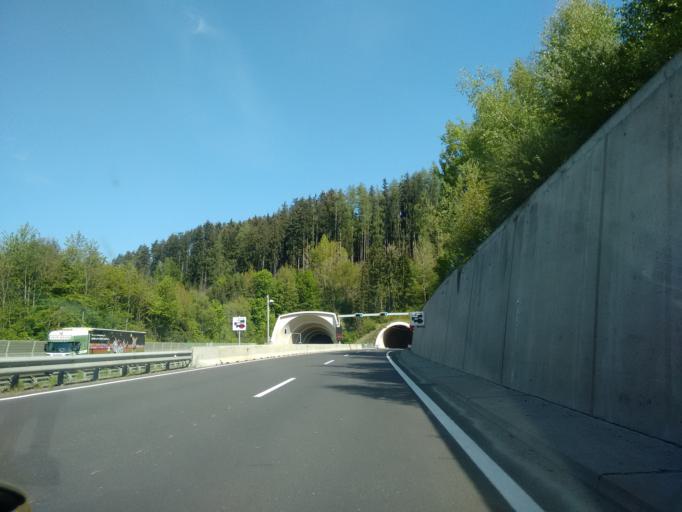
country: AT
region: Styria
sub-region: Politischer Bezirk Leoben
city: Leoben
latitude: 47.3698
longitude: 15.1050
